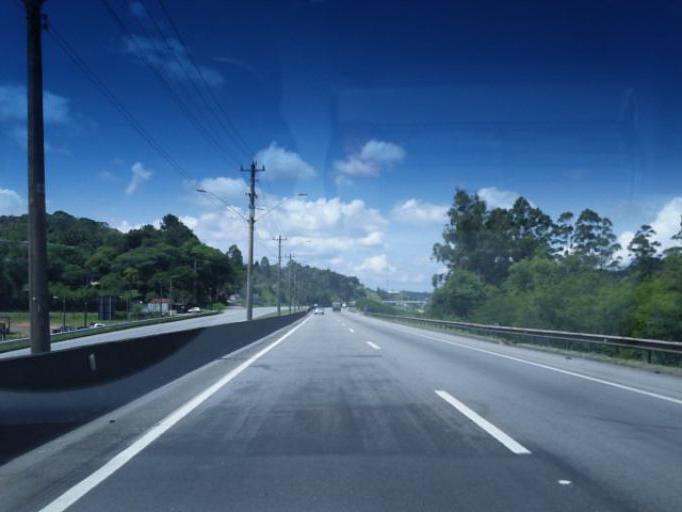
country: BR
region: Sao Paulo
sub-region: Sao Lourenco Da Serra
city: Sao Lourenco da Serra
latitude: -23.8766
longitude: -46.9676
